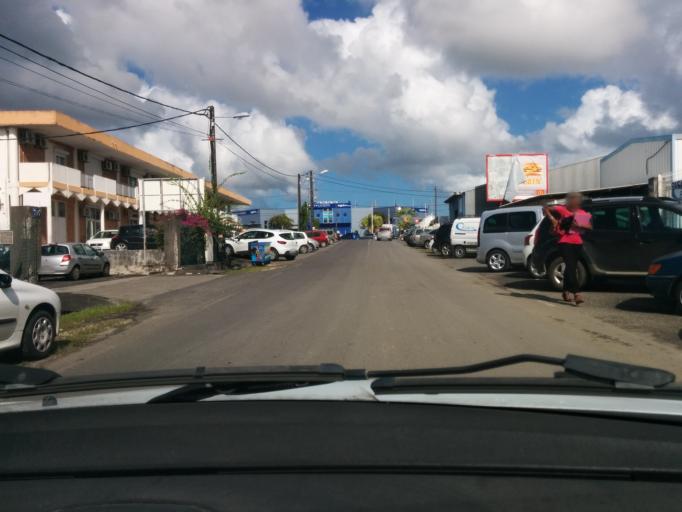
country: GP
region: Guadeloupe
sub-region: Guadeloupe
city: Pointe-a-Pitre
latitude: 16.2400
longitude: -61.5634
